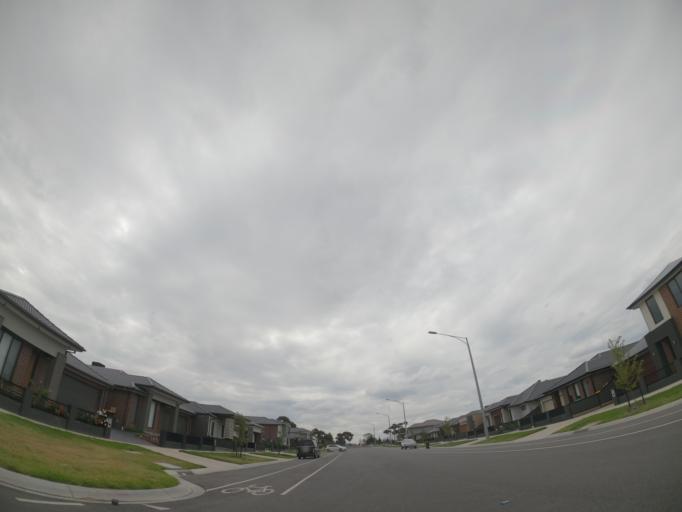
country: AU
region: Victoria
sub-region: Hume
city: Craigieburn
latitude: -37.5659
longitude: 144.8962
